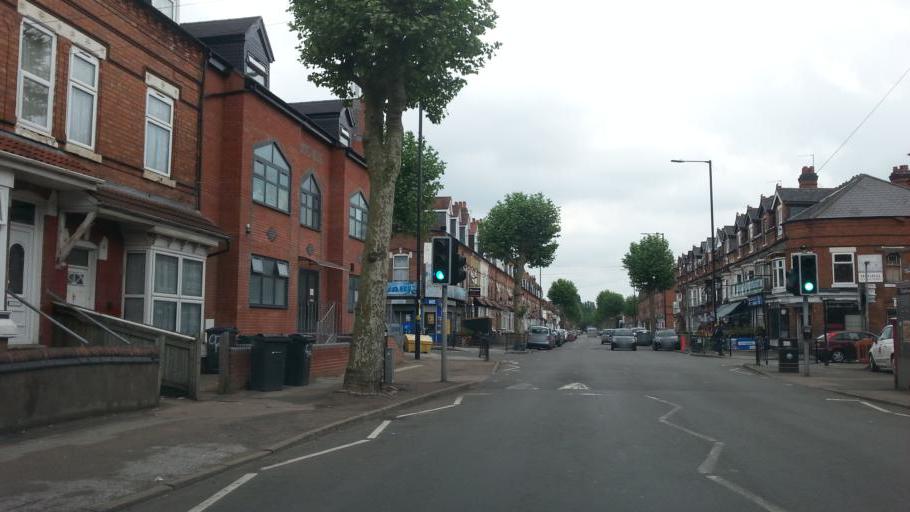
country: GB
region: England
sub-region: City and Borough of Birmingham
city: Birmingham
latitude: 52.4593
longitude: -1.8672
